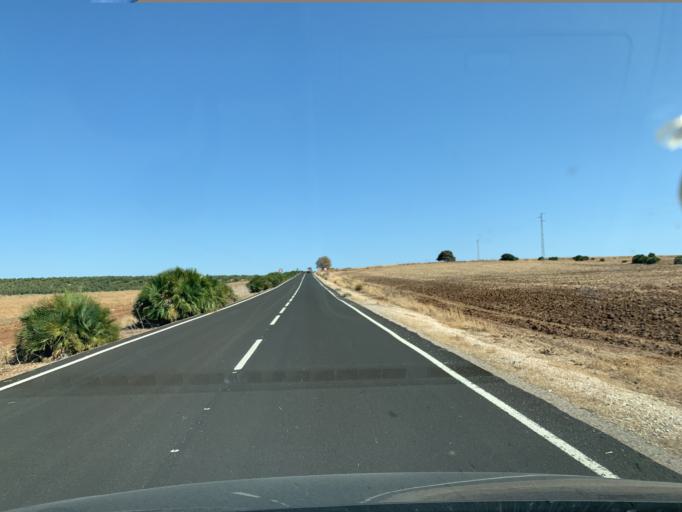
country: ES
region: Andalusia
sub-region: Provincia de Sevilla
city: La Lantejuela
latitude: 37.3325
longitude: -5.3112
